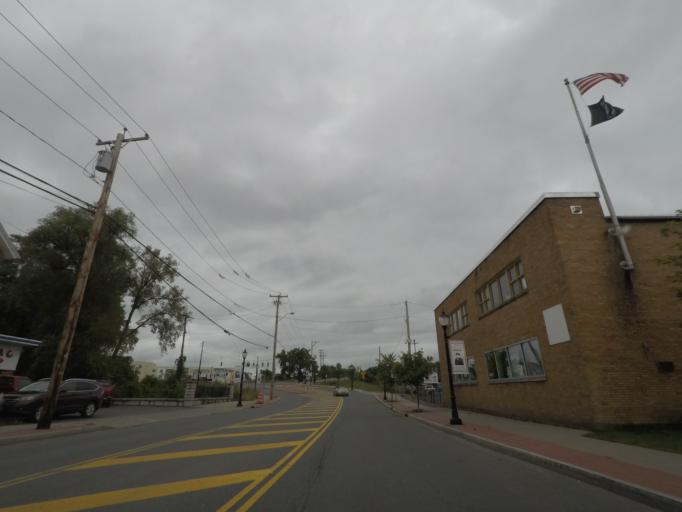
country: US
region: New York
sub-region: Rensselaer County
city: Rensselaer
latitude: 42.6433
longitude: -73.7426
